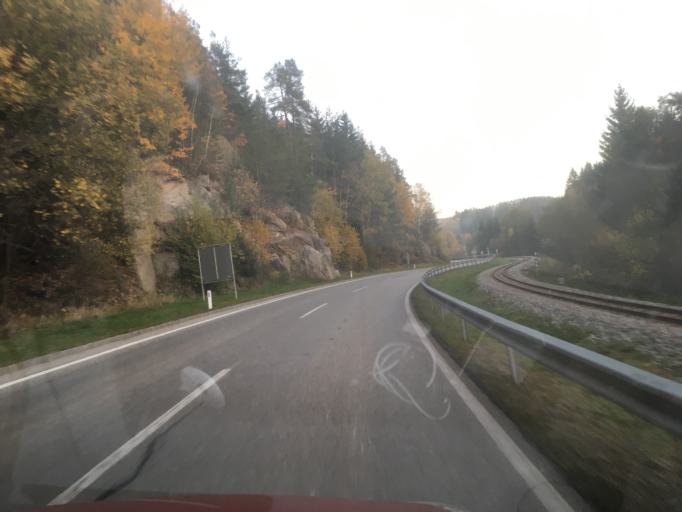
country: AT
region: Lower Austria
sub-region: Politischer Bezirk Zwettl
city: Langschlag
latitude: 48.5810
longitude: 14.8756
